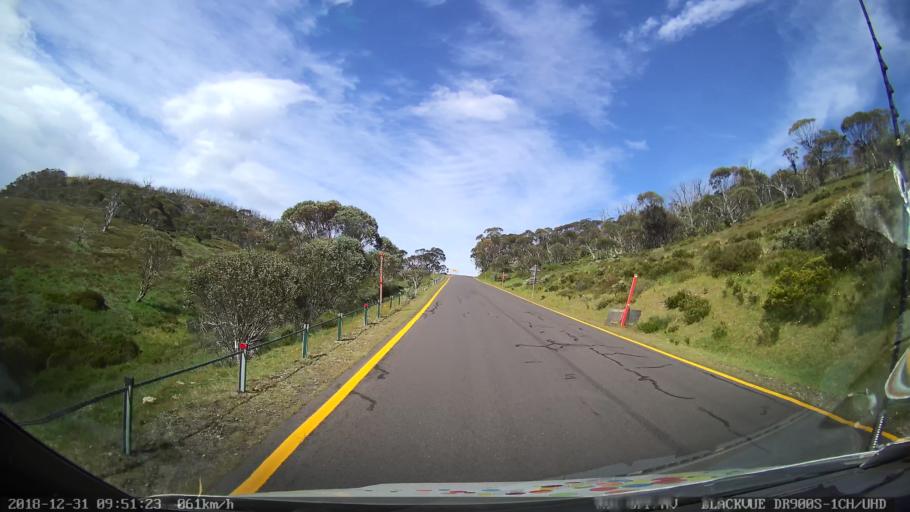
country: AU
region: New South Wales
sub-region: Snowy River
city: Jindabyne
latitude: -36.5227
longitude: 148.2626
